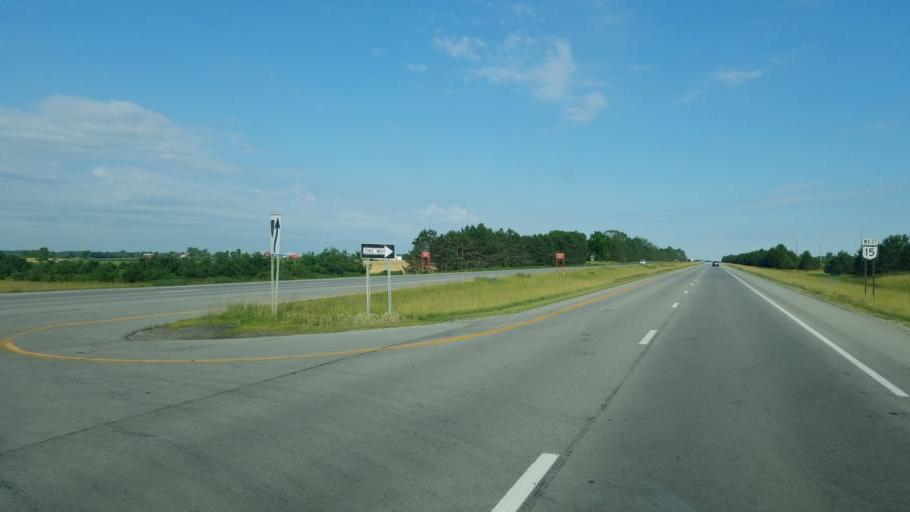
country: US
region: Ohio
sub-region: Wyandot County
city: Carey
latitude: 40.9567
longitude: -83.4462
